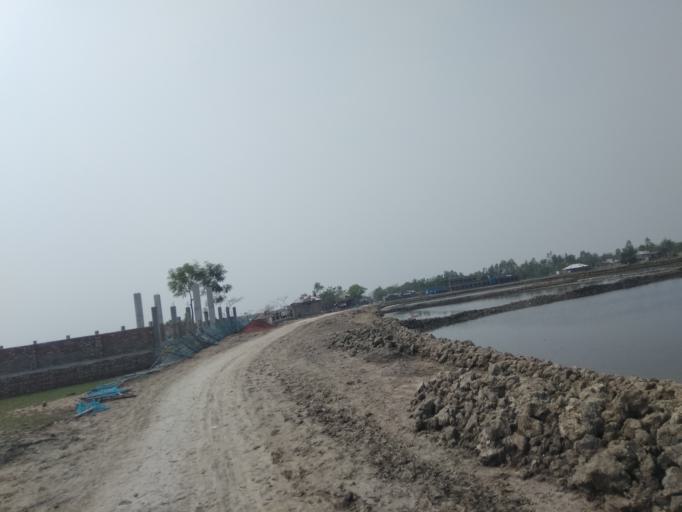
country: IN
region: West Bengal
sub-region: North 24 Parganas
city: Taki
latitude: 22.3476
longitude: 89.2222
